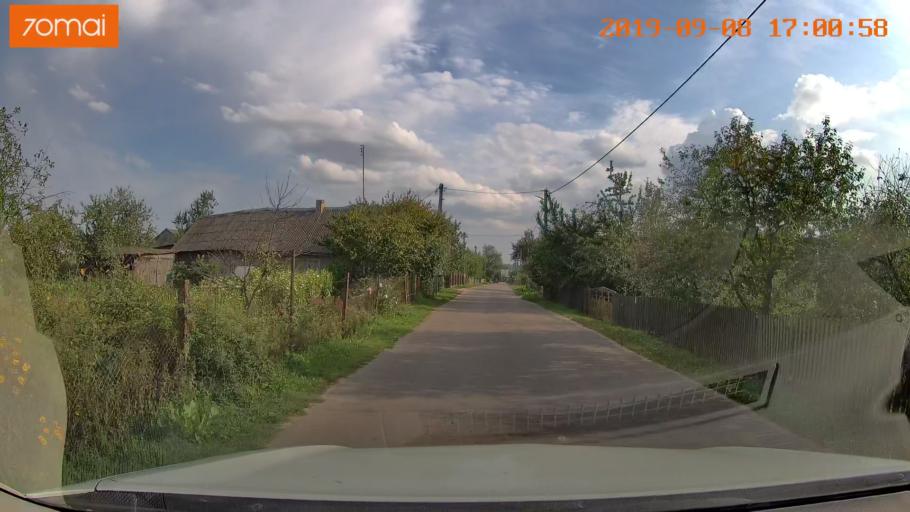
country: BY
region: Grodnenskaya
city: Hrodna
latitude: 53.7130
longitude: 23.9331
